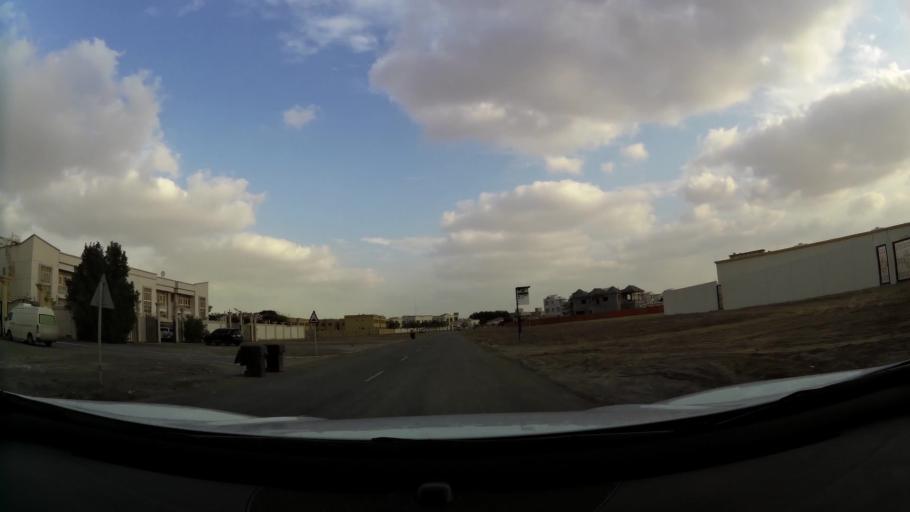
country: AE
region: Abu Dhabi
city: Abu Dhabi
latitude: 24.3602
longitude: 54.5568
